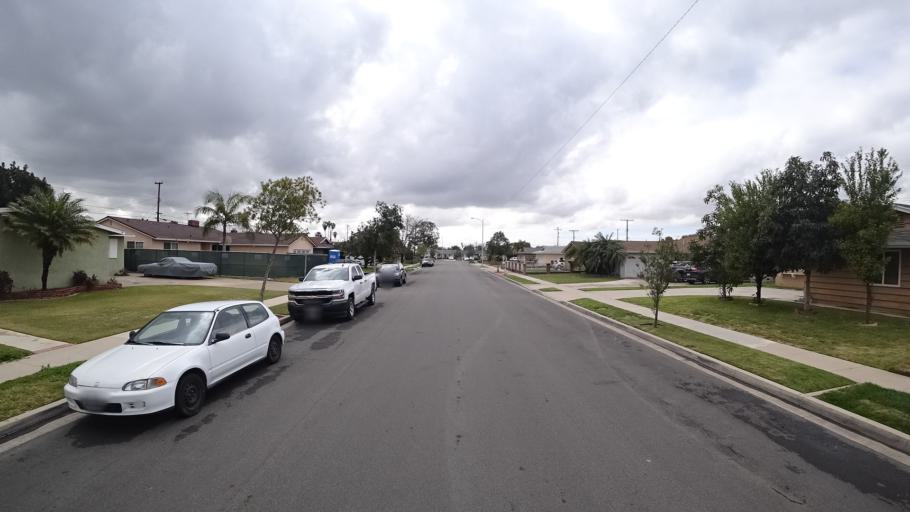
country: US
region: California
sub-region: Orange County
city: Anaheim
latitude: 33.8309
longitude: -117.9528
